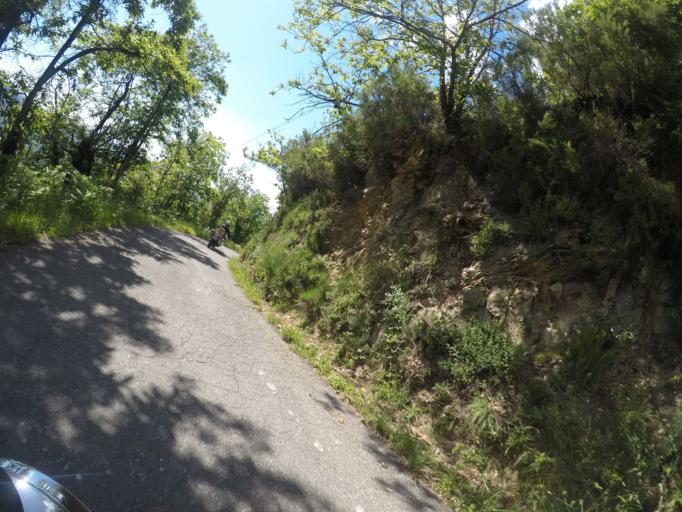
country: IT
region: Tuscany
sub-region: Provincia di Massa-Carrara
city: Casola in Lunigiana
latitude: 44.1784
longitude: 10.1704
